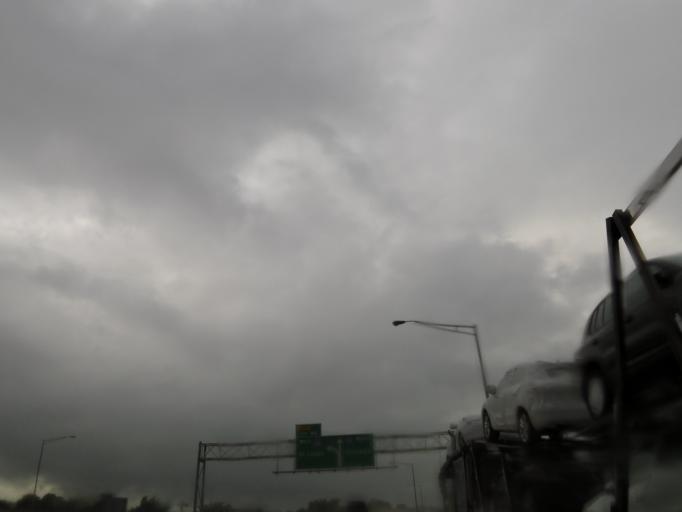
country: US
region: Illinois
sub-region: Jefferson County
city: Mount Vernon
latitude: 38.3258
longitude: -88.9555
